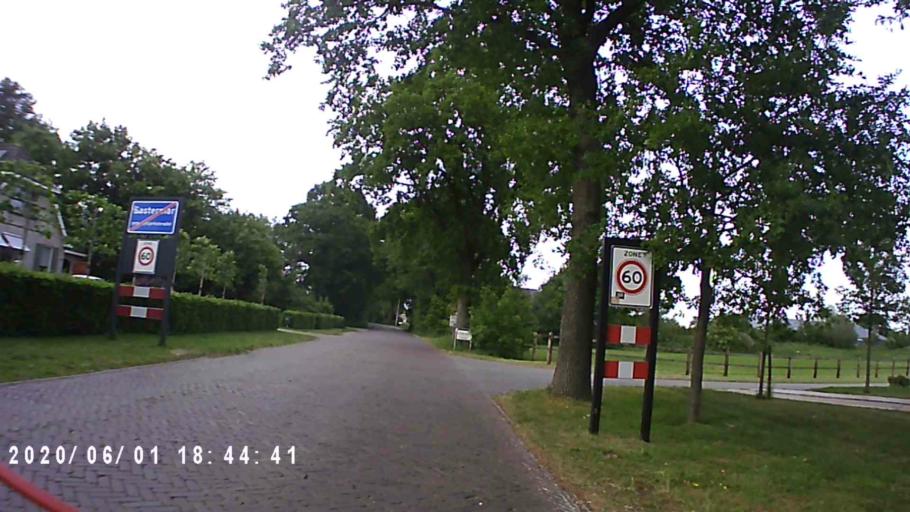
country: NL
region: Friesland
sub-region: Gemeente Tytsjerksteradiel
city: Eastermar
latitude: 53.1769
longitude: 6.0667
